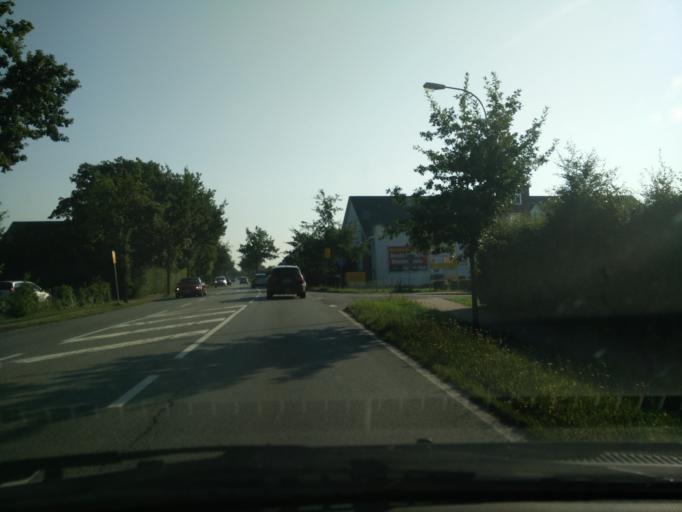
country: DE
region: Schleswig-Holstein
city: Tornesch
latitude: 53.7020
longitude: 9.7268
